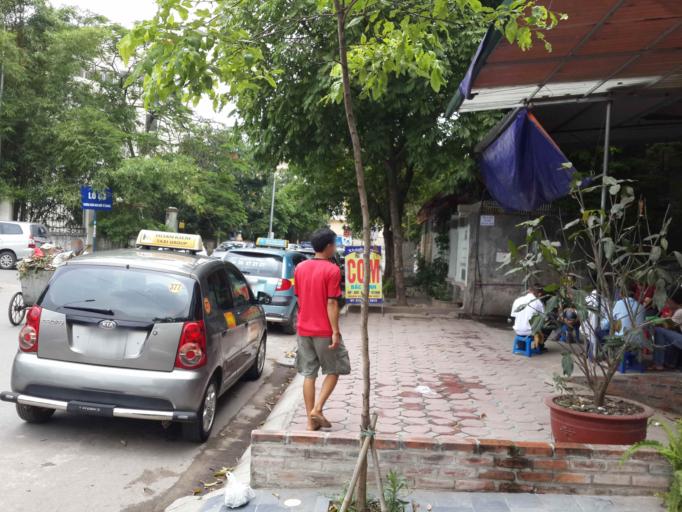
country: VN
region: Ha Noi
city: Cau Giay
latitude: 21.0180
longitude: 105.7970
